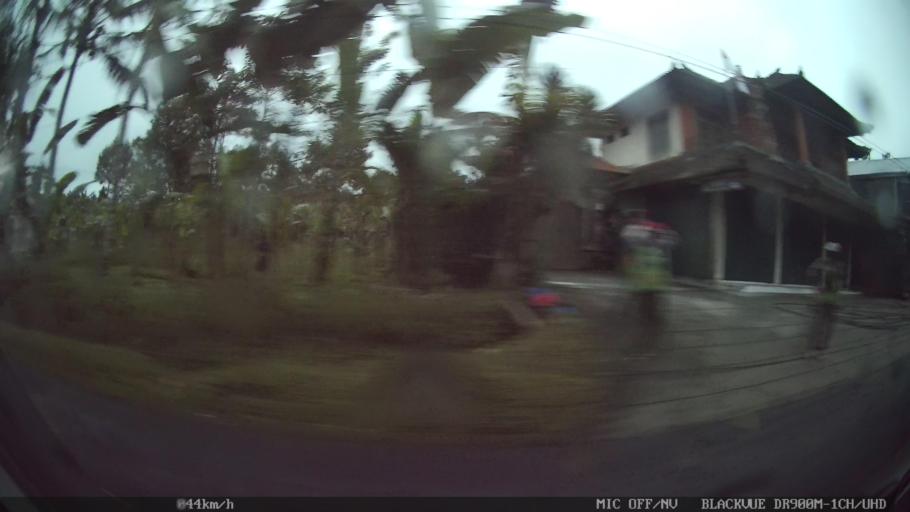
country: ID
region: Bali
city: Banjar Ponggang
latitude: -8.3792
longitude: 115.2663
